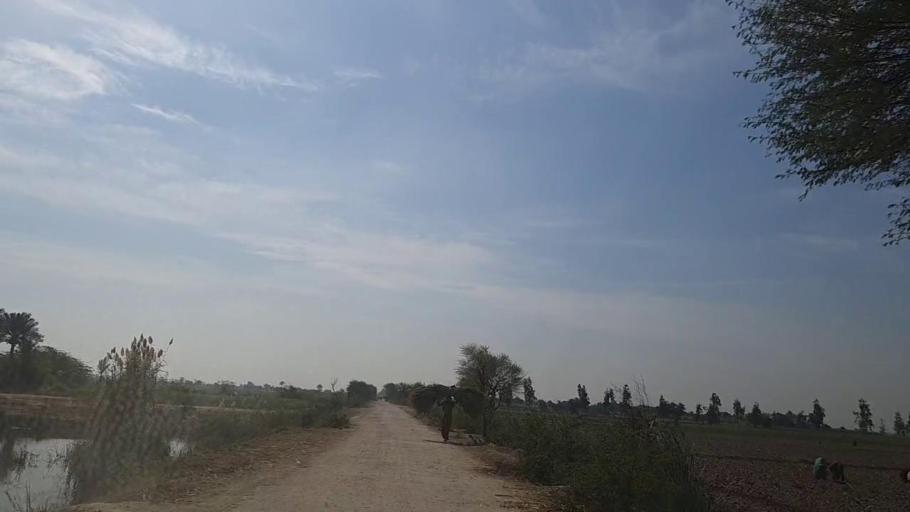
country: PK
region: Sindh
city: Mirpur Khas
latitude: 25.4783
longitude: 68.9640
